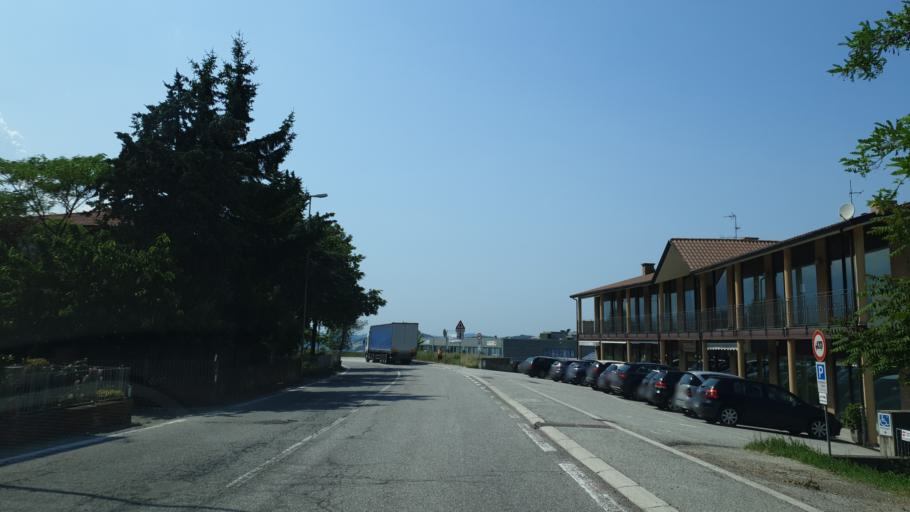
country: SM
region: Acquaviva
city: Acquaviva
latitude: 43.9466
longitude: 12.4268
